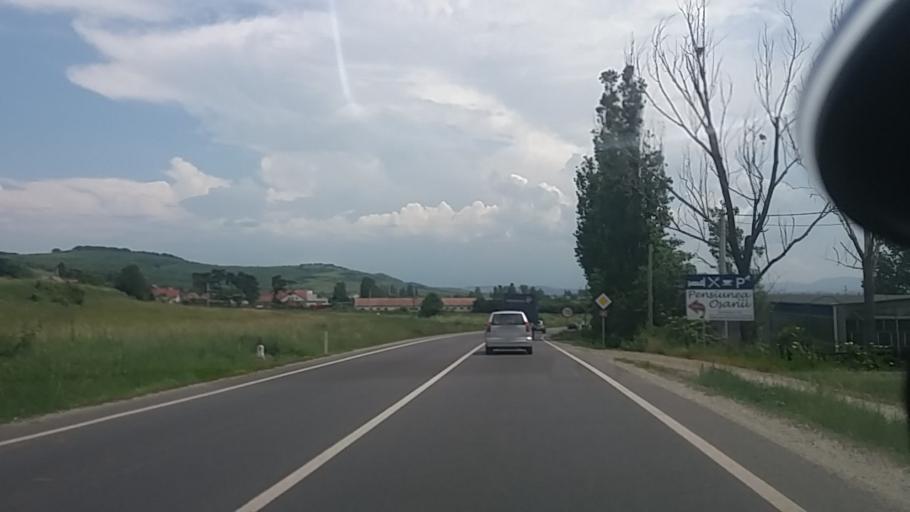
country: RO
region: Sibiu
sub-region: Comuna Sura Mare
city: Sura Mare
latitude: 45.8411
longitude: 24.1492
